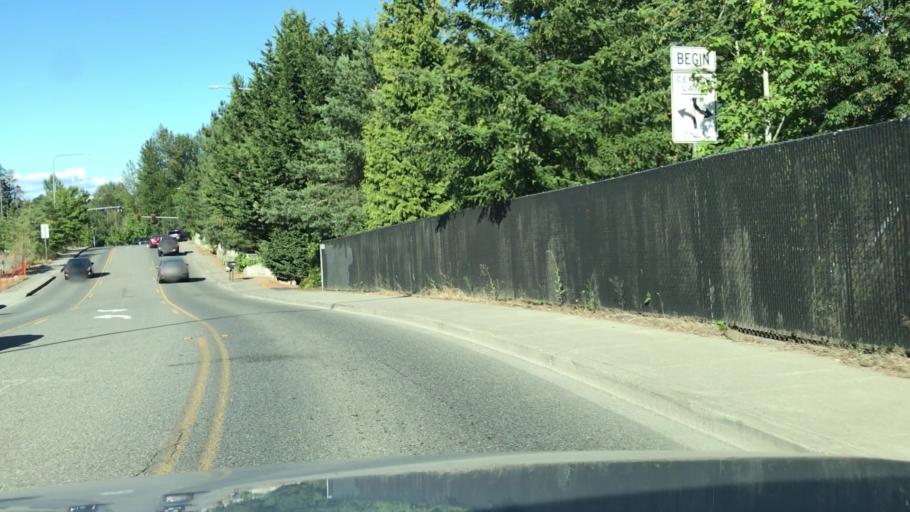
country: US
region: Washington
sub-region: King County
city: Issaquah
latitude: 47.5494
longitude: -122.0246
